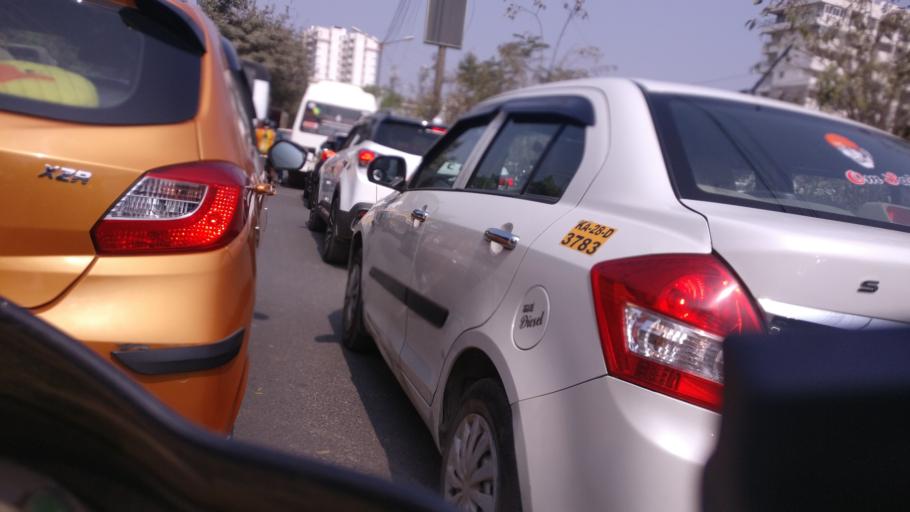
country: IN
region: Karnataka
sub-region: Bangalore Urban
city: Bangalore
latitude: 12.9151
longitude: 77.6749
